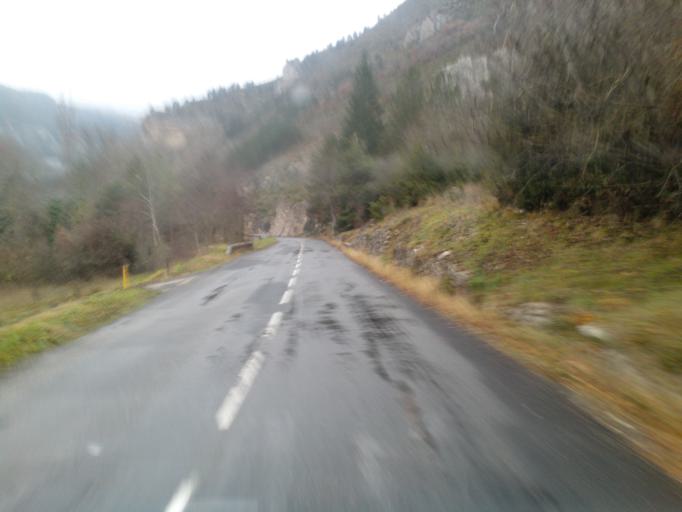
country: FR
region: Languedoc-Roussillon
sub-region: Departement de la Lozere
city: Florac
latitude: 44.3417
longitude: 3.5027
